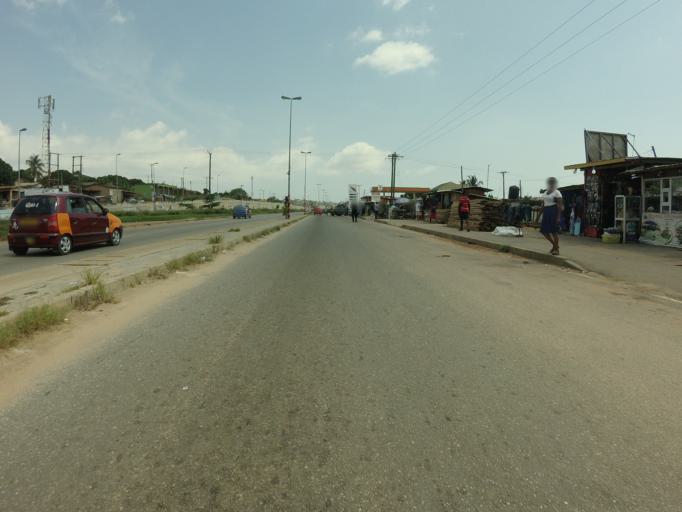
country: GH
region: Greater Accra
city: Gbawe
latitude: 5.6256
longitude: -0.3070
